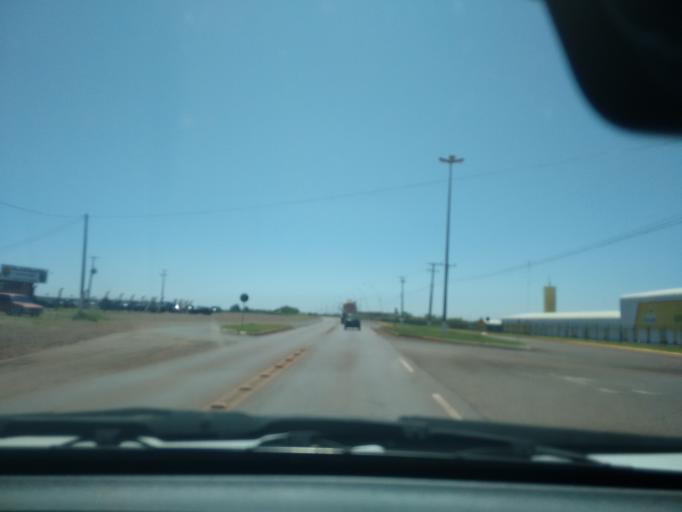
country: BR
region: Parana
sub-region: Marechal Candido Rondon
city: Marechal Candido Rondon
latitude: -24.5576
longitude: -54.1062
